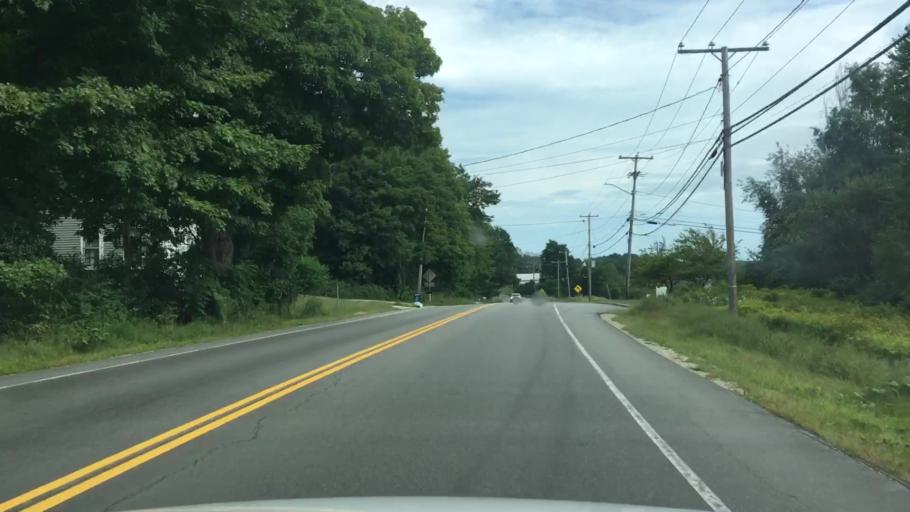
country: US
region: New Hampshire
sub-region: Strafford County
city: Madbury
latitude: 43.1889
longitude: -70.9163
